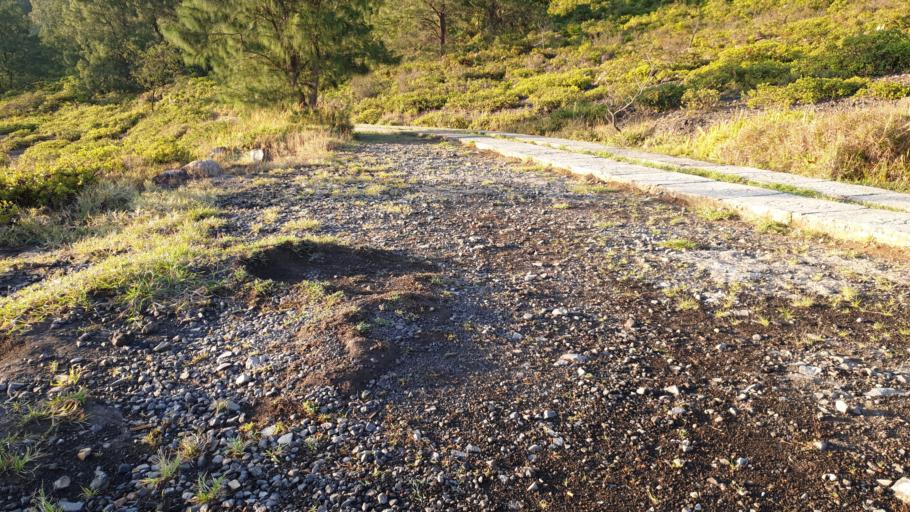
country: ID
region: East Nusa Tenggara
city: Koanara
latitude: -8.7668
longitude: 121.8125
